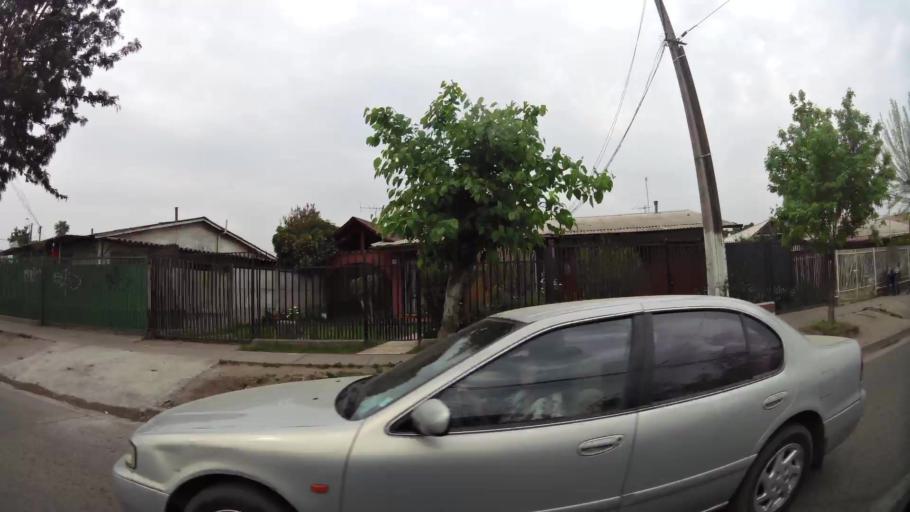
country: CL
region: Santiago Metropolitan
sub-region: Provincia de Chacabuco
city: Chicureo Abajo
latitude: -33.2001
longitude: -70.6751
